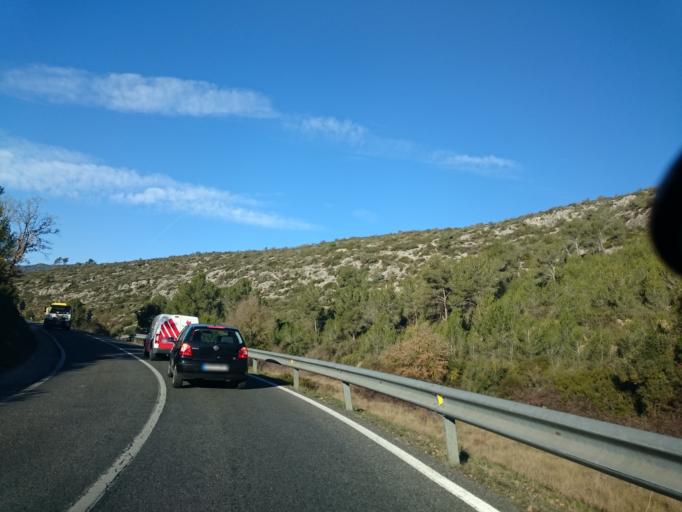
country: ES
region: Catalonia
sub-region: Provincia de Barcelona
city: Sant Pere de Ribes
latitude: 41.2905
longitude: 1.7365
